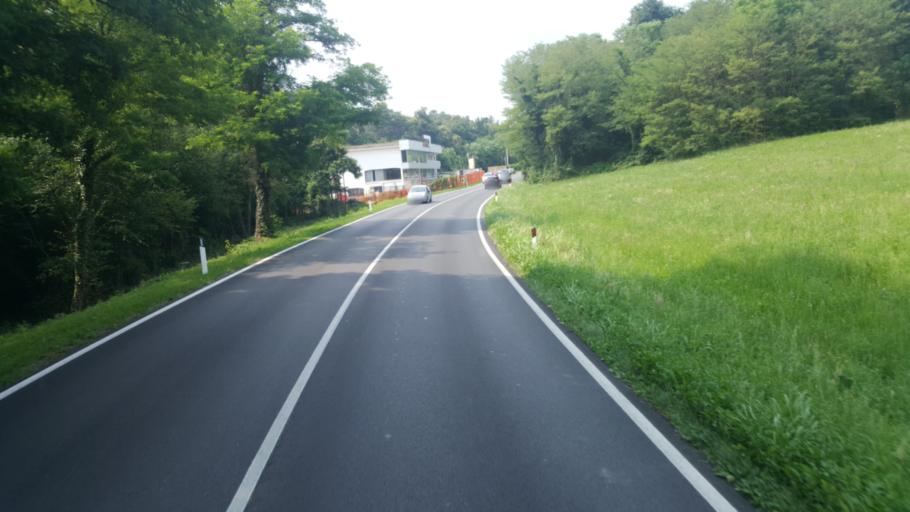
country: IT
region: Lombardy
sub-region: Provincia di Como
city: Beregazzo
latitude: 45.7622
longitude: 8.9625
